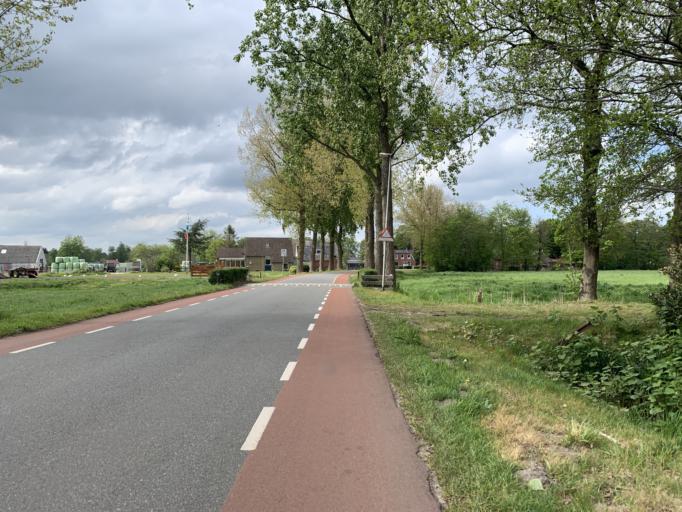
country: NL
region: Groningen
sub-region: Gemeente Haren
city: Haren
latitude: 53.2123
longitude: 6.6426
